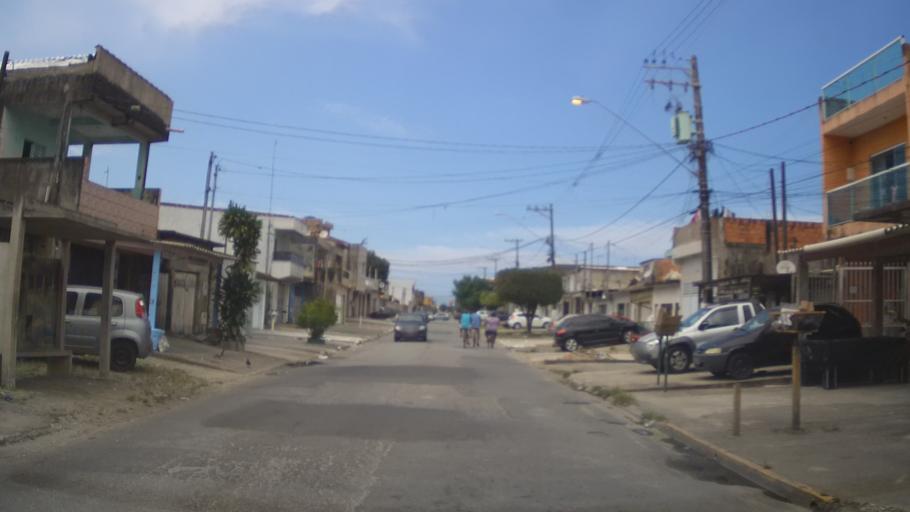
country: BR
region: Sao Paulo
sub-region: Praia Grande
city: Praia Grande
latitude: -24.0158
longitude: -46.4893
